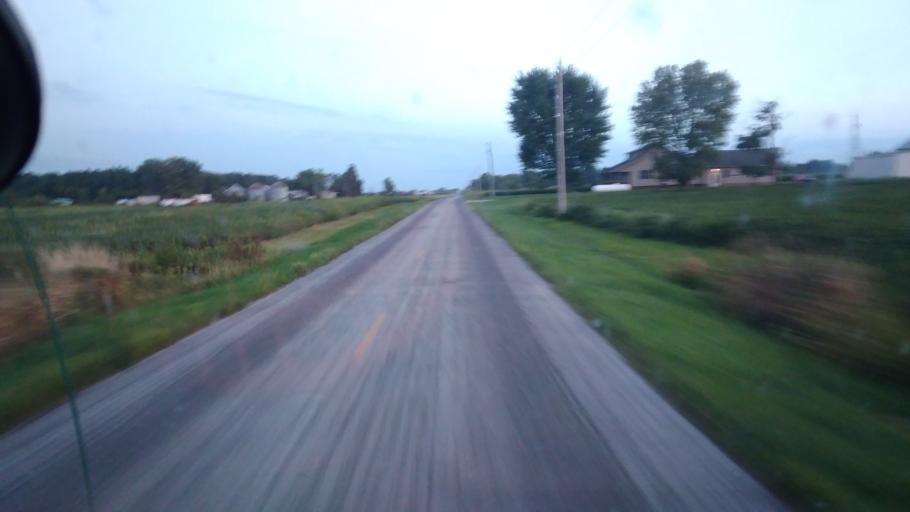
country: US
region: Ohio
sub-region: Hardin County
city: Kenton
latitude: 40.6398
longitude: -83.4579
